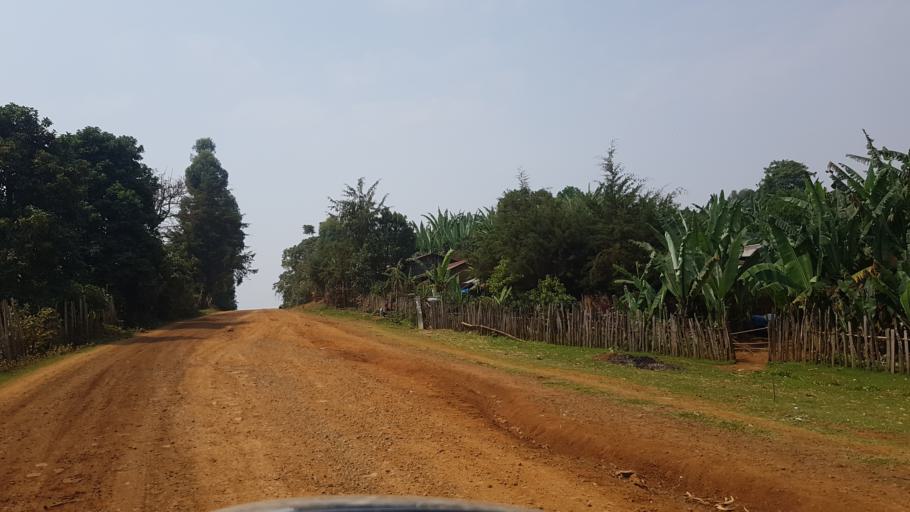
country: ET
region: Oromiya
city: Gore
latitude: 7.7994
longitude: 35.4574
